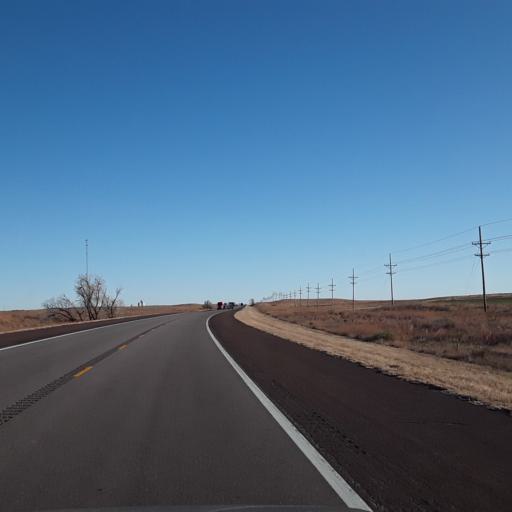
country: US
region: Kansas
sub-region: Meade County
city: Plains
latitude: 37.1747
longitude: -100.7313
